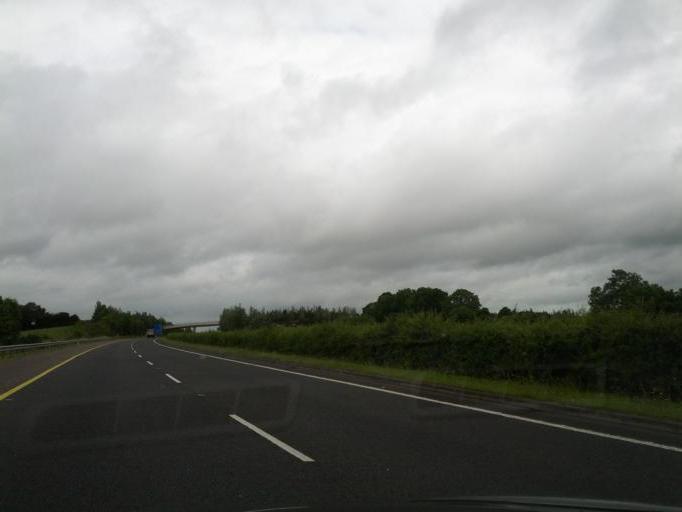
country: IE
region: Munster
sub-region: An Clar
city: Newmarket on Fergus
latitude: 52.7339
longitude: -8.8887
